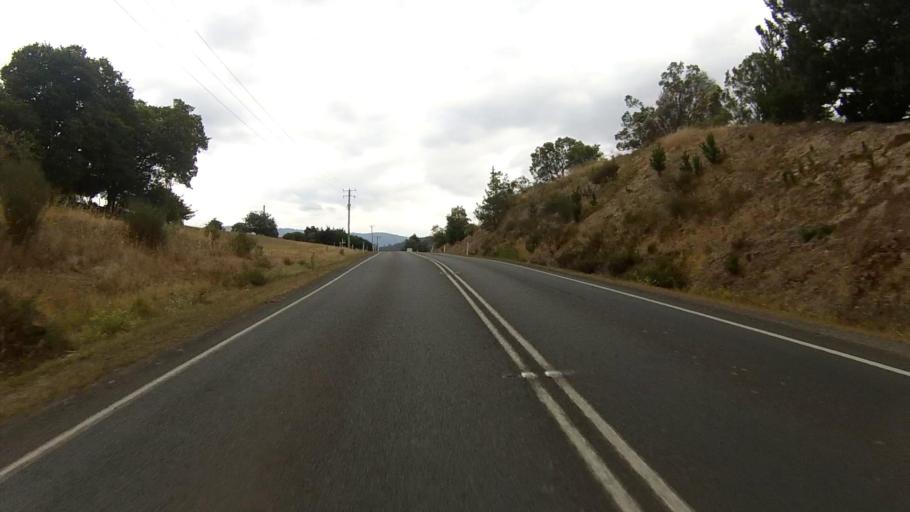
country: AU
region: Tasmania
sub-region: Huon Valley
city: Franklin
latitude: -43.1127
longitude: 147.0365
